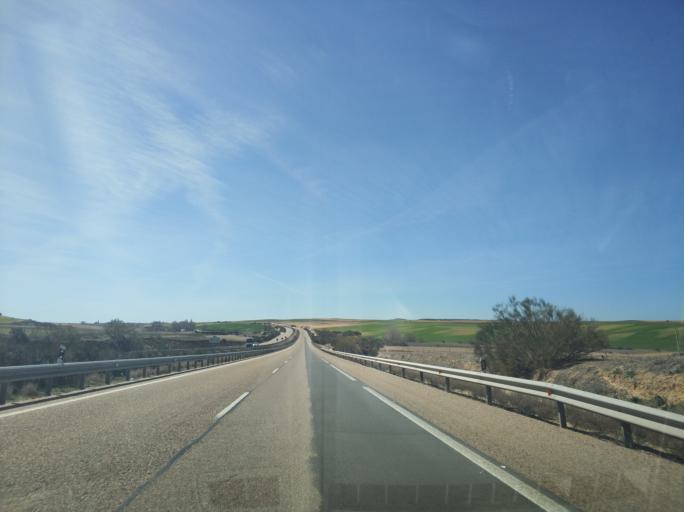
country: ES
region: Castille and Leon
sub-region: Provincia de Zamora
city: Castrillo de la Guarena
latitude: 41.2000
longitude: -5.3410
